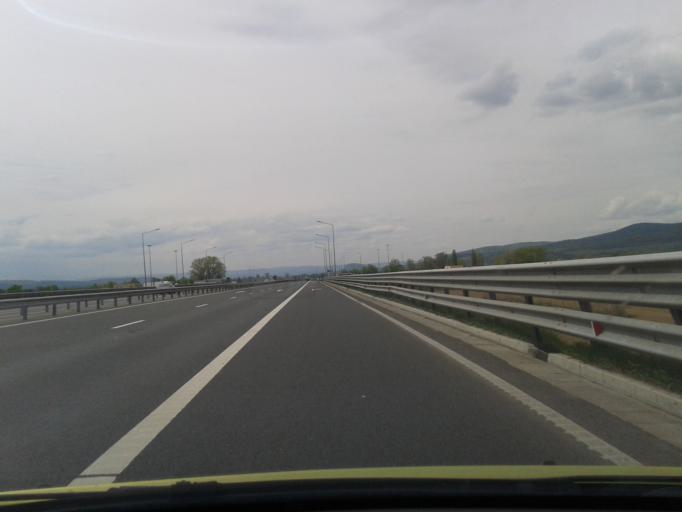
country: RO
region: Hunedoara
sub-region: Comuna Turdas
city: Pricaz
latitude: 45.8785
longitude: 23.1963
